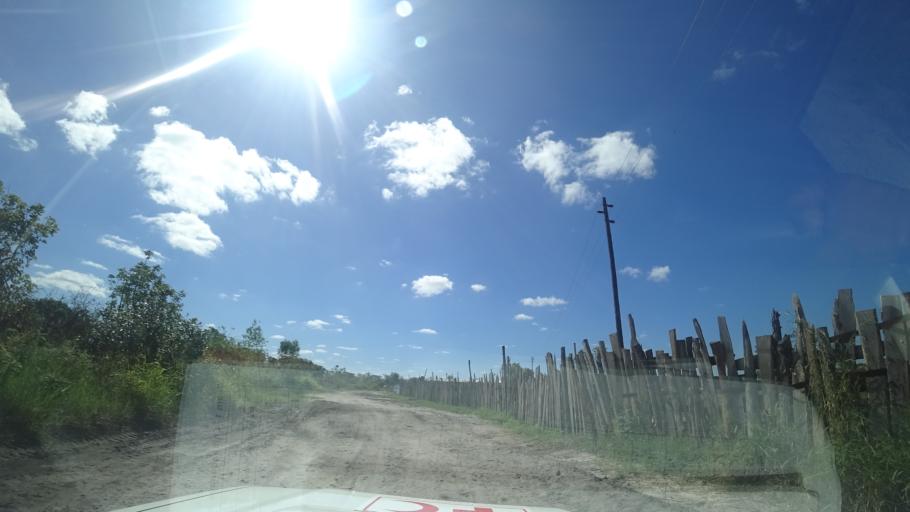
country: MZ
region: Sofala
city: Dondo
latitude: -19.5028
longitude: 34.6123
